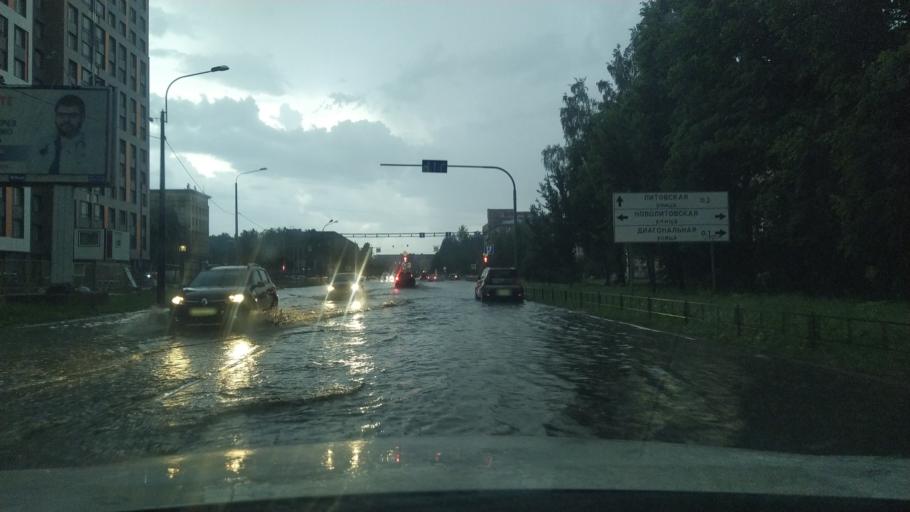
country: RU
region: Leningrad
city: Sampsonievskiy
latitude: 59.9824
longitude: 30.3534
